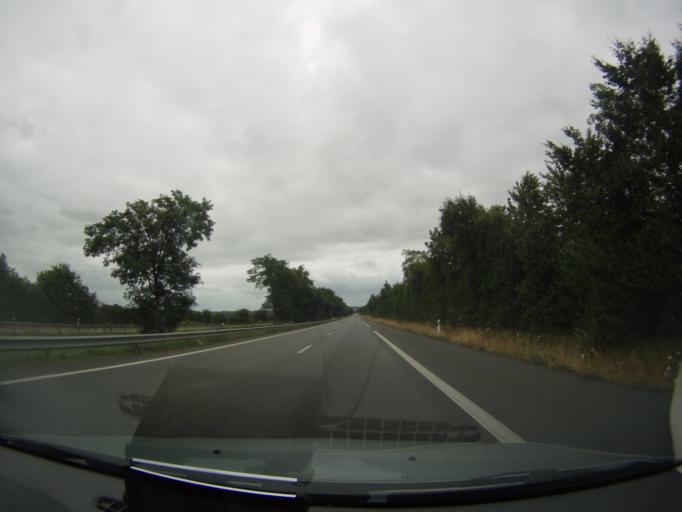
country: FR
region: Brittany
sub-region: Departement d'Ille-et-Vilaine
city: Grand-Fougeray
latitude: 47.7159
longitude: -1.7082
